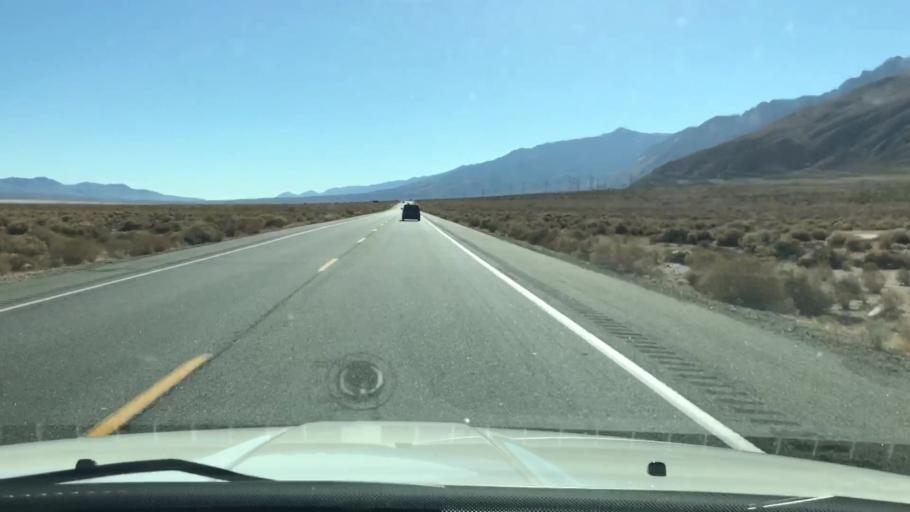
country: US
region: California
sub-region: Inyo County
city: Lone Pine
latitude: 36.3708
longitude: -118.0238
